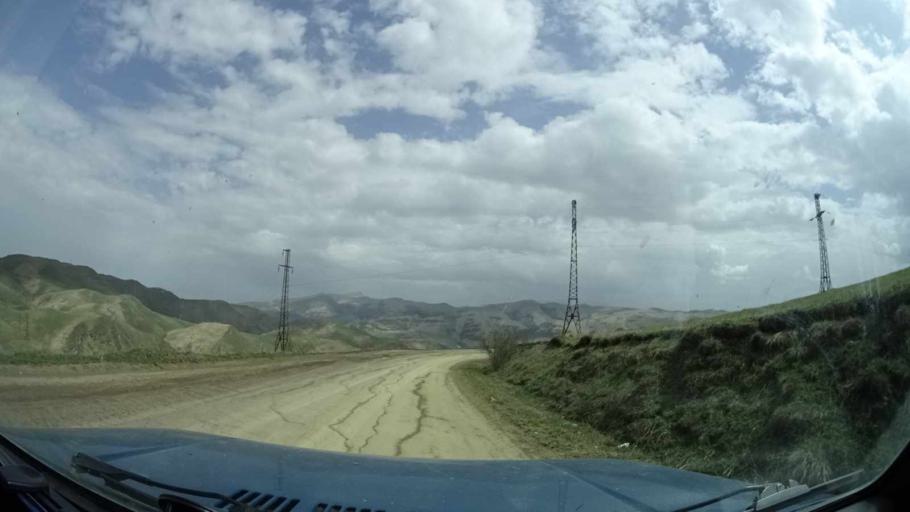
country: RU
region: Dagestan
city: Kubachi
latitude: 42.0816
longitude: 47.5576
